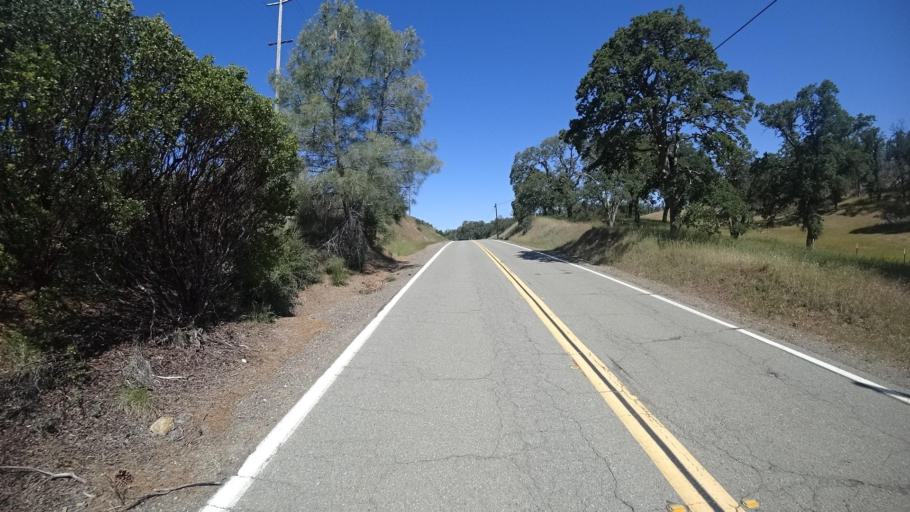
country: US
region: California
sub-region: Lake County
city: Hidden Valley Lake
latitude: 38.8819
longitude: -122.4500
